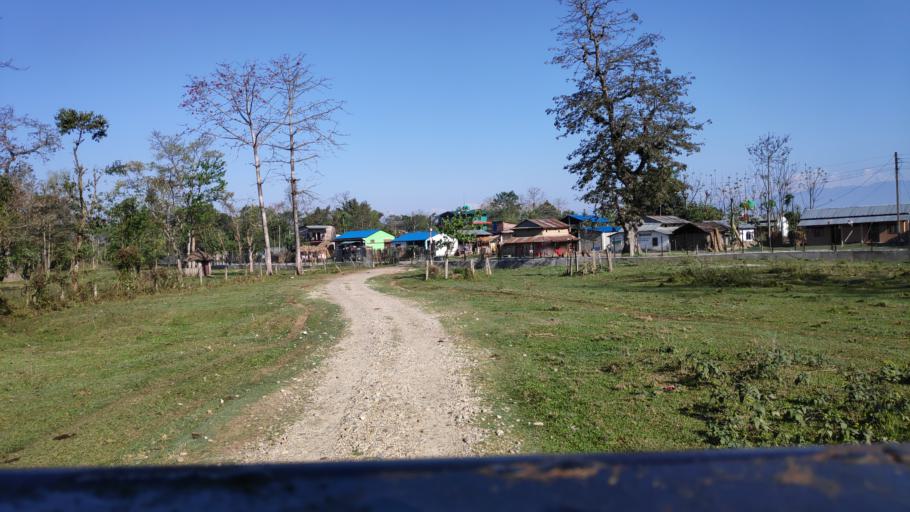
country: NP
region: Central Region
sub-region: Narayani Zone
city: Bharatpur
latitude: 27.5664
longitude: 84.5219
